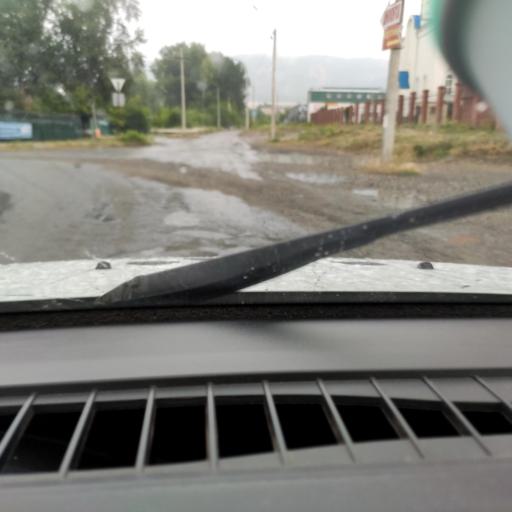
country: RU
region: Chelyabinsk
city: Miass
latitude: 55.0504
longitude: 60.0961
